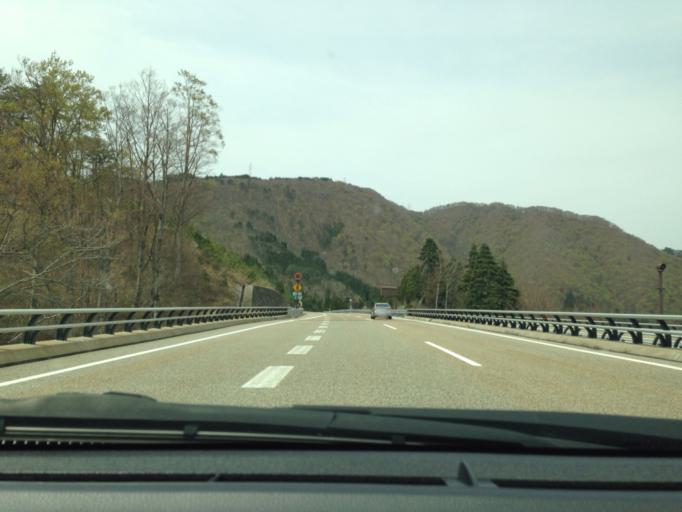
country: JP
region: Toyama
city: Fukumitsu
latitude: 36.2665
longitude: 136.8980
